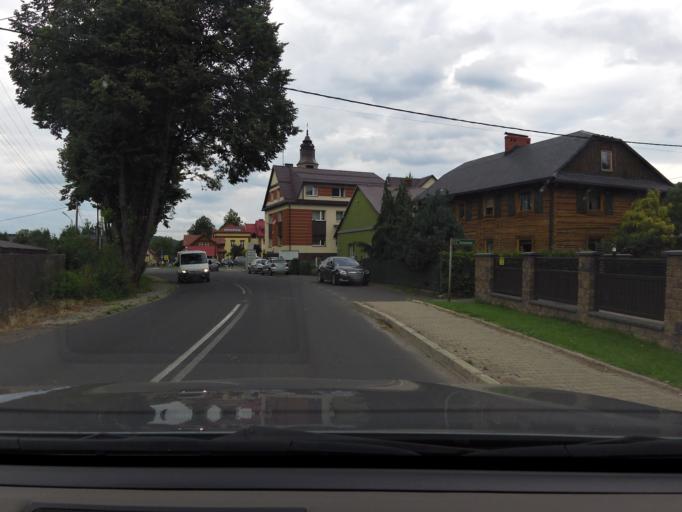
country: PL
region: Silesian Voivodeship
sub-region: Powiat zywiecki
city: Ujsoly
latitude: 49.4771
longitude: 19.1447
